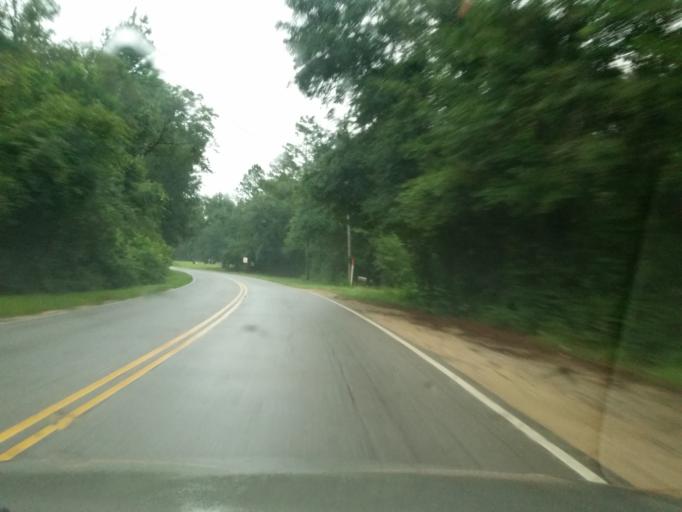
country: US
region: Florida
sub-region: Escambia County
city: Cantonment
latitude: 30.6044
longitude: -87.3660
